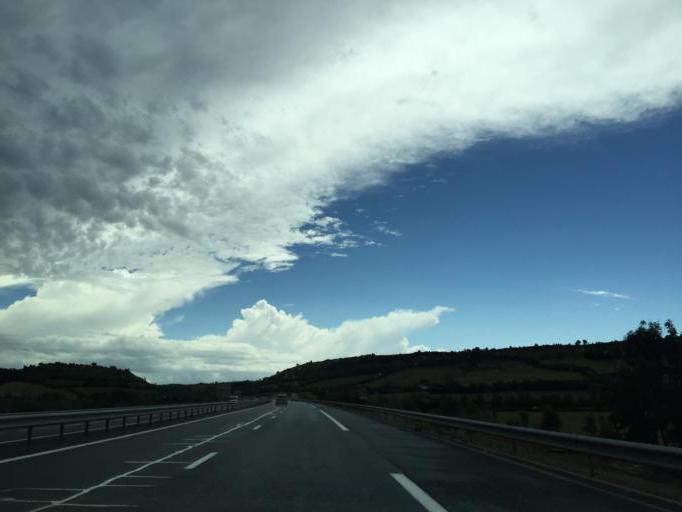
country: FR
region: Midi-Pyrenees
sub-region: Departement de l'Aveyron
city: Severac-le-Chateau
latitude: 44.3284
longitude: 3.0869
